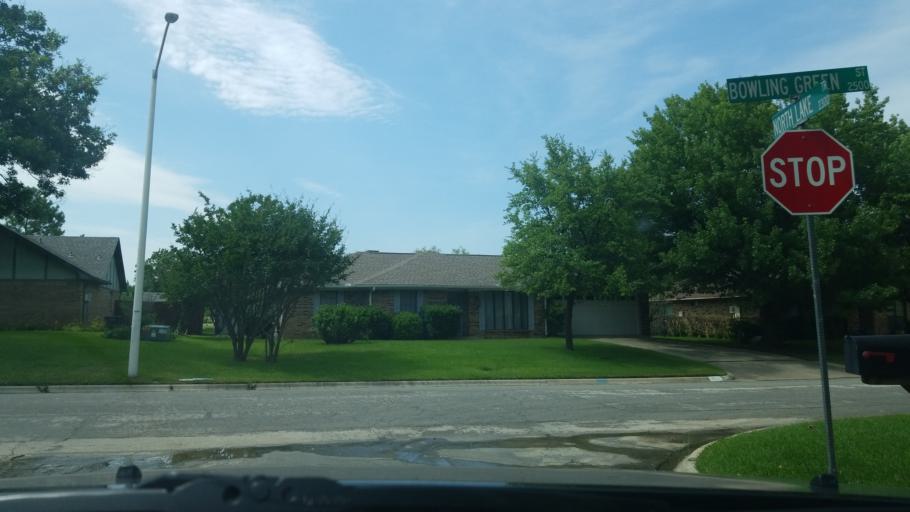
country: US
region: Texas
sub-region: Denton County
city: Denton
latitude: 33.2393
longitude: -97.1525
